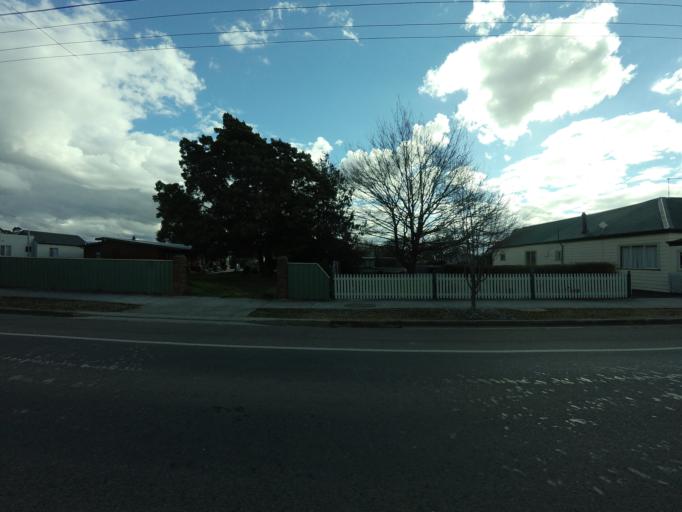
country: AU
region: Tasmania
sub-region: Northern Midlands
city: Longford
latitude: -41.6836
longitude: 147.0809
